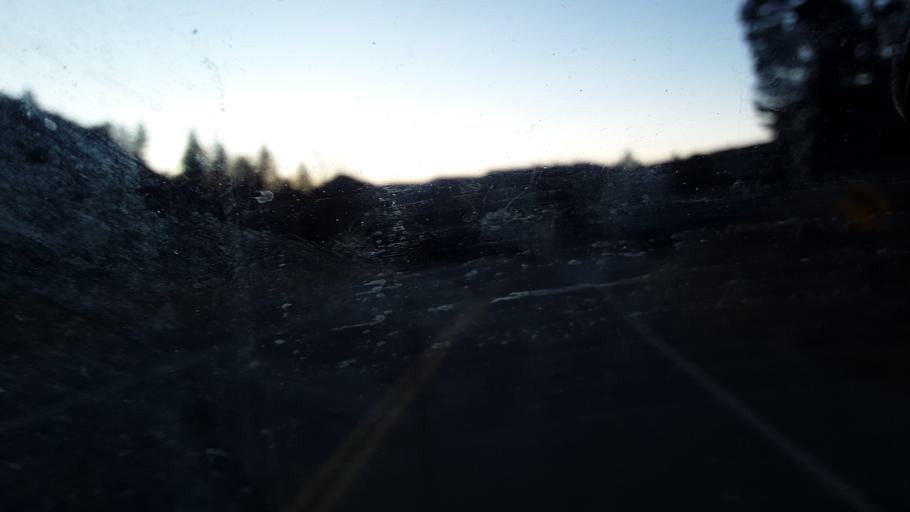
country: US
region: Colorado
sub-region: La Plata County
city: Durango
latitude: 37.3055
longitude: -107.8281
